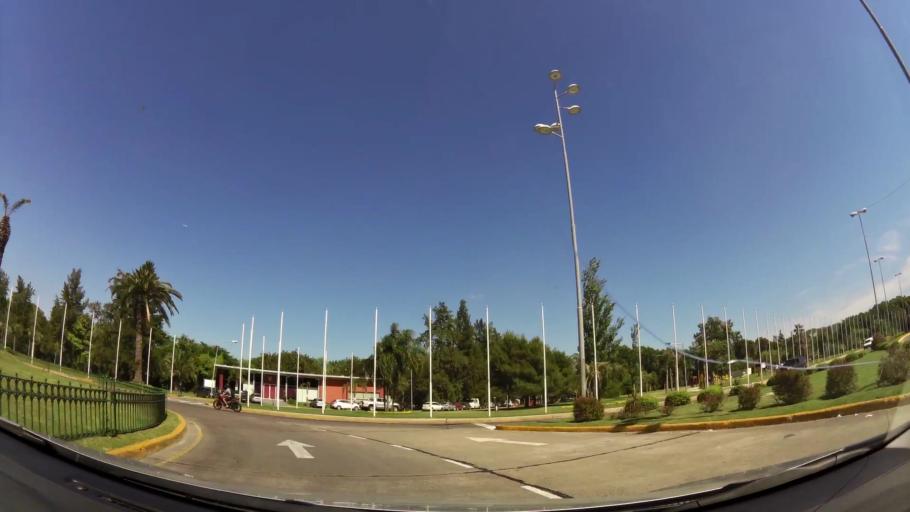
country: AR
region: Buenos Aires
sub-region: Partido de Tigre
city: Tigre
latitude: -34.4252
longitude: -58.5826
